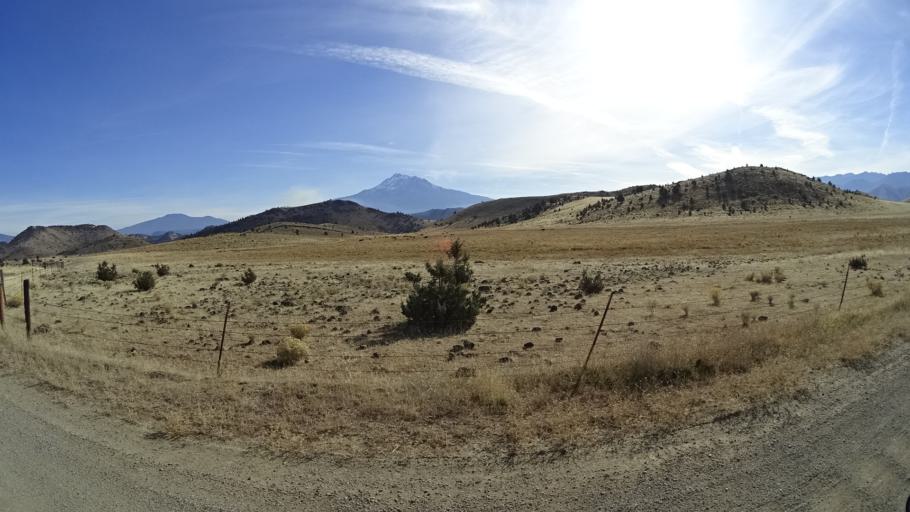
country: US
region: California
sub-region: Siskiyou County
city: Weed
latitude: 41.5323
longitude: -122.4696
